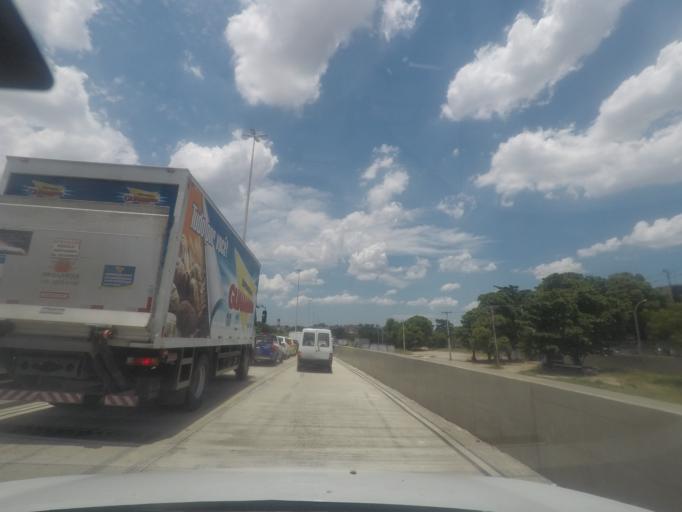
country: BR
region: Rio de Janeiro
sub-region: Sao Joao De Meriti
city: Sao Joao de Meriti
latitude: -22.8321
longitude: -43.3540
